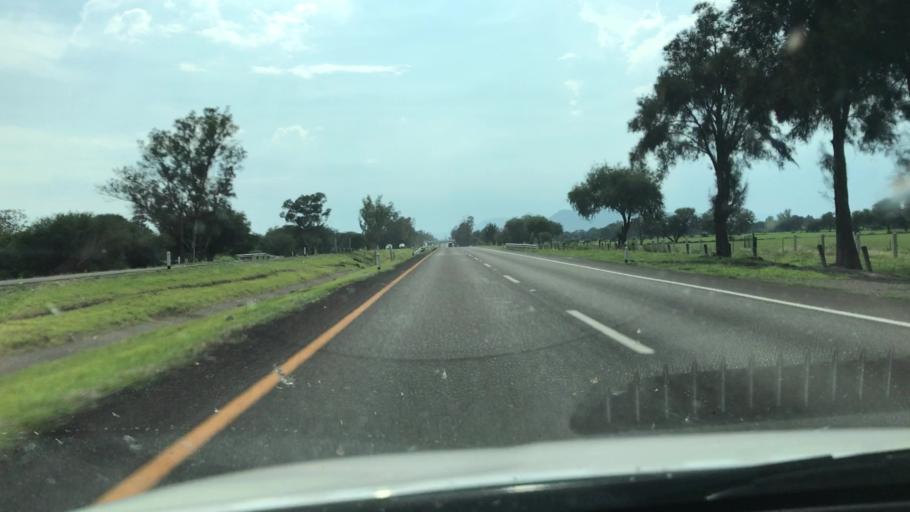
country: MX
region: Jalisco
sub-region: Ocotlan
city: Joconoxtle (La Tuna)
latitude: 20.3778
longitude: -102.6814
